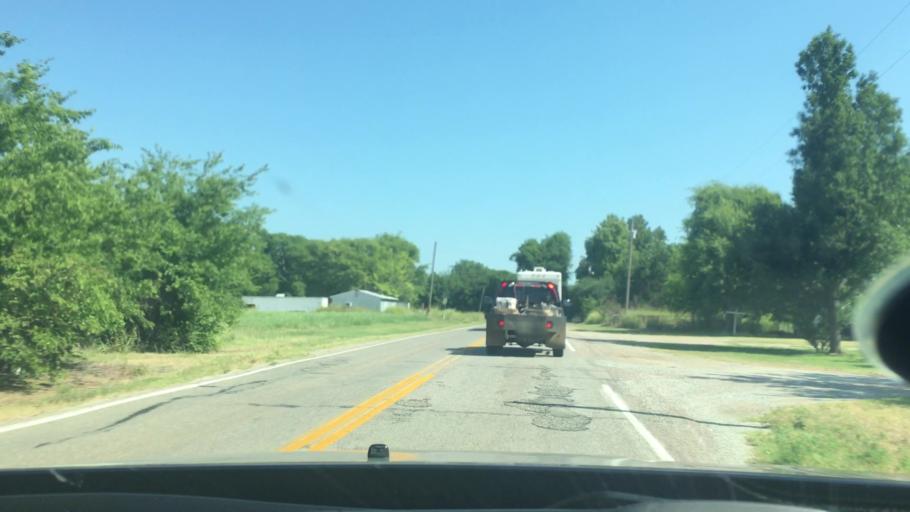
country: US
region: Oklahoma
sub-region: Johnston County
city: Tishomingo
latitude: 34.2014
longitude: -96.5428
